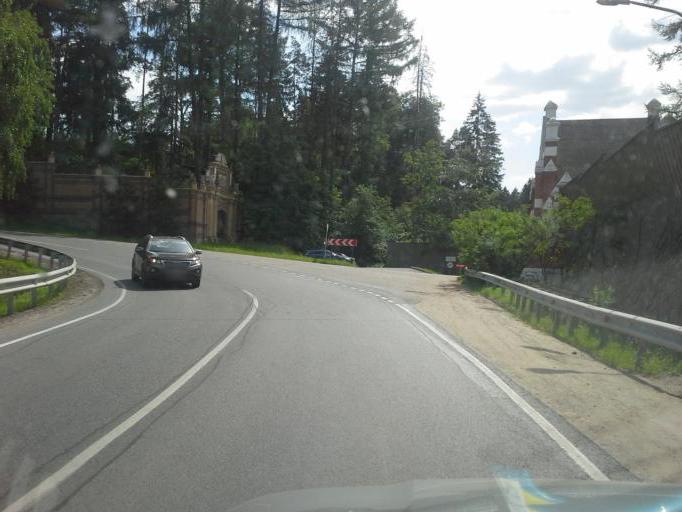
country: RU
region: Moskovskaya
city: Barvikha
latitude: 55.7186
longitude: 37.2642
